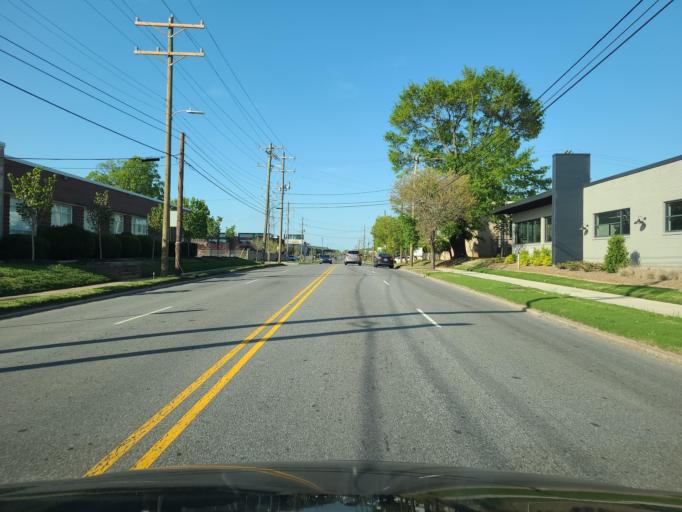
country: US
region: North Carolina
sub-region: Mecklenburg County
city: Charlotte
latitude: 35.2422
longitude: -80.8339
